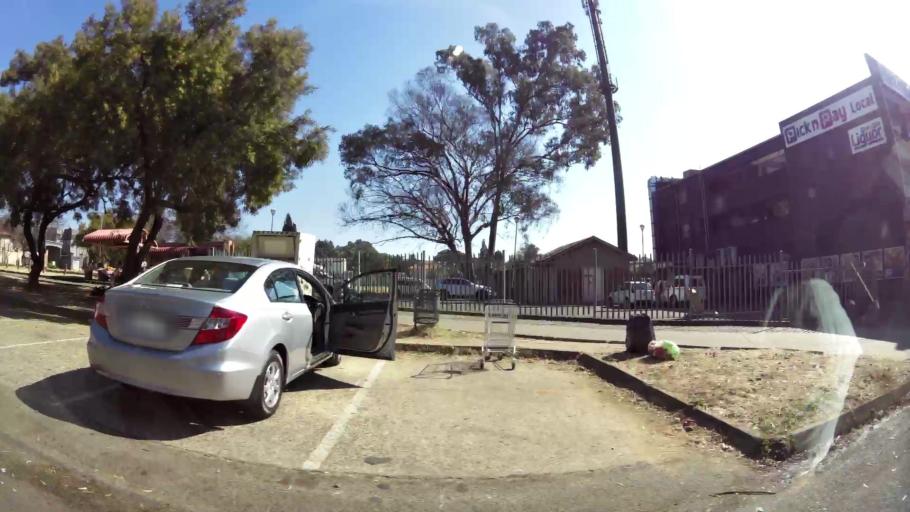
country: ZA
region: Gauteng
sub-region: City of Johannesburg Metropolitan Municipality
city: Modderfontein
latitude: -26.1582
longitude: 28.1242
